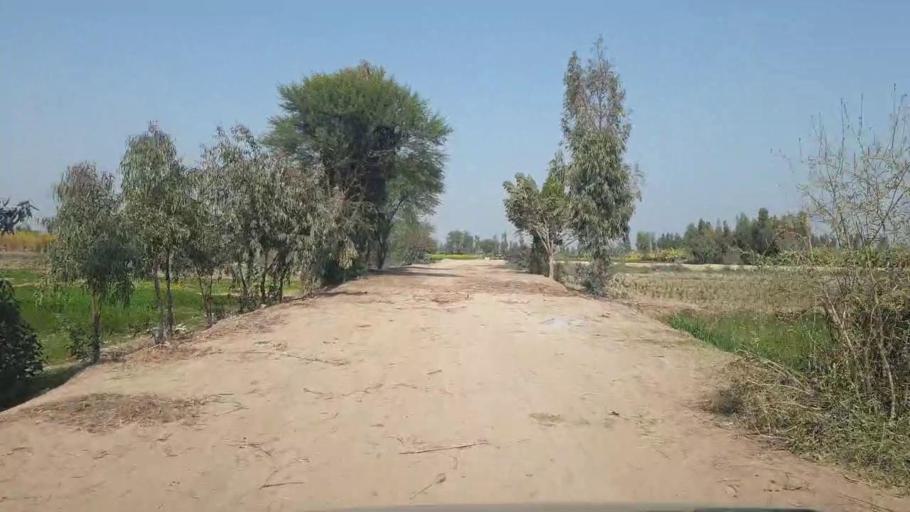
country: PK
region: Sindh
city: Tando Adam
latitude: 25.8004
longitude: 68.6299
